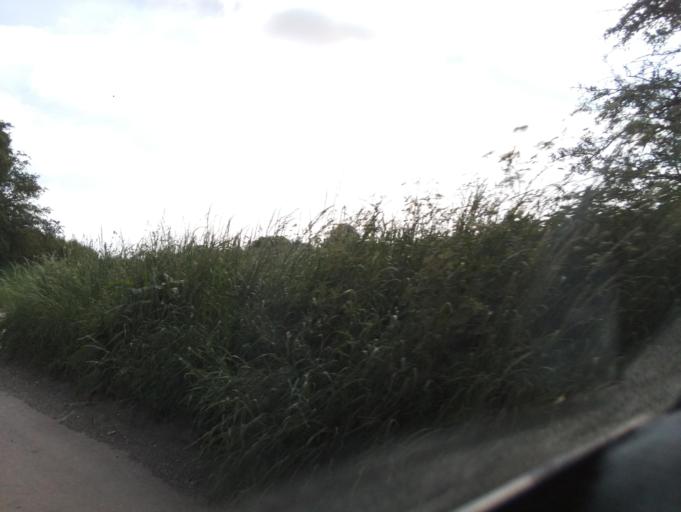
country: GB
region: England
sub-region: Wiltshire
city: Collingbourne Kingston
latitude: 51.2751
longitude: -1.7087
